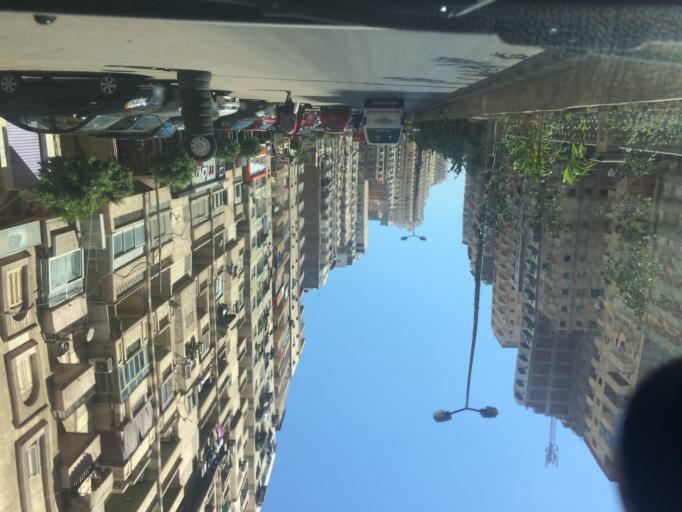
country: EG
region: Alexandria
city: Alexandria
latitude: 31.2537
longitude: 29.9863
